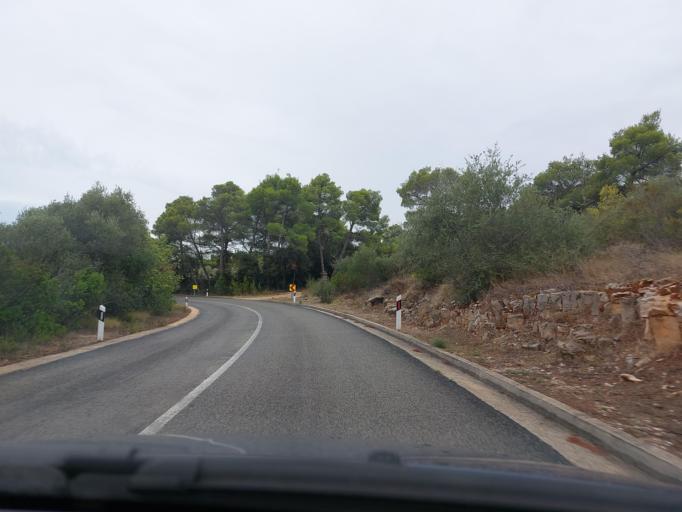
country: HR
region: Dubrovacko-Neretvanska
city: Smokvica
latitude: 42.7668
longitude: 16.8719
